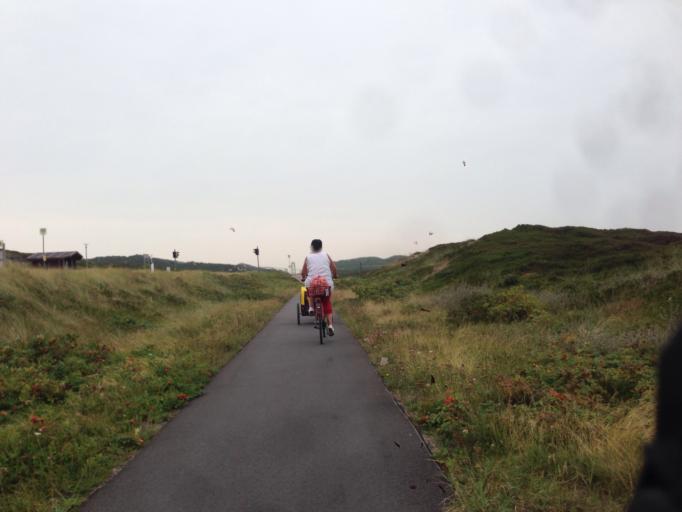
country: DE
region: Schleswig-Holstein
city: Westerland
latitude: 54.8011
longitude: 8.2881
